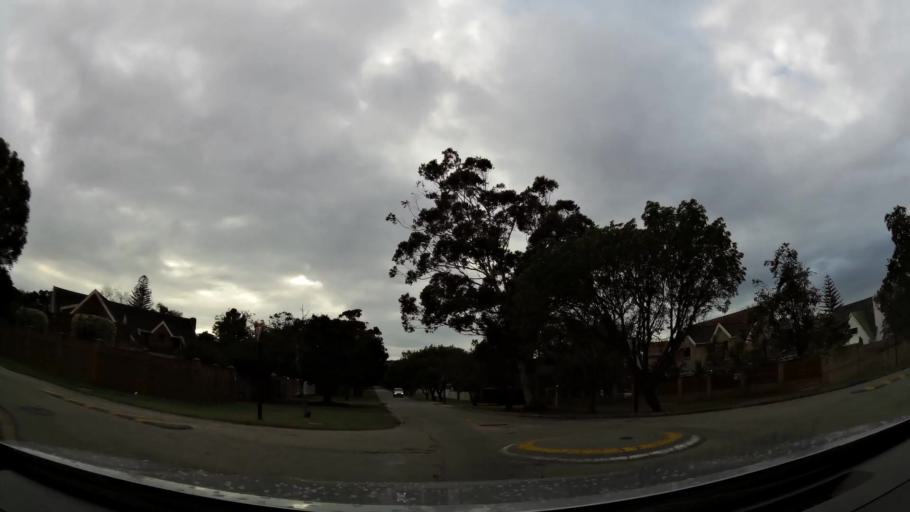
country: ZA
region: Eastern Cape
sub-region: Nelson Mandela Bay Metropolitan Municipality
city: Port Elizabeth
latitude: -33.9777
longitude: 25.5741
